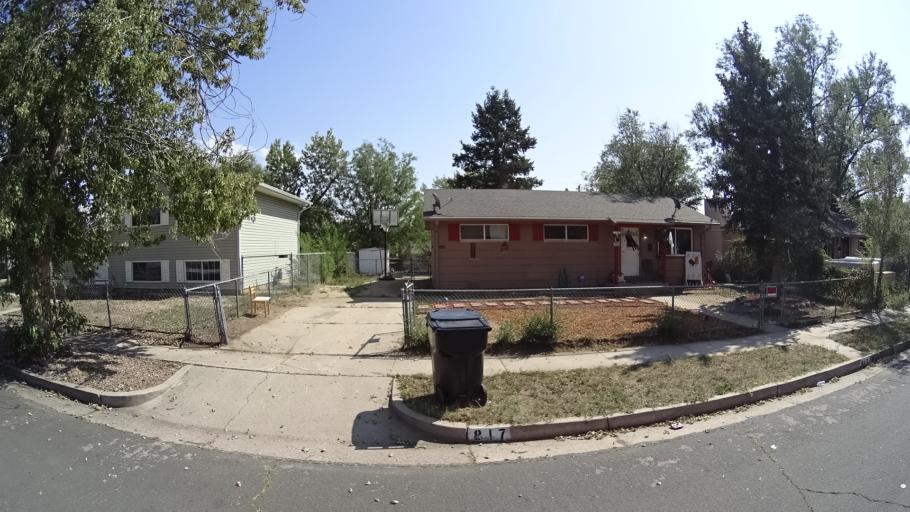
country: US
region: Colorado
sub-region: El Paso County
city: Colorado Springs
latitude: 38.8200
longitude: -104.7835
